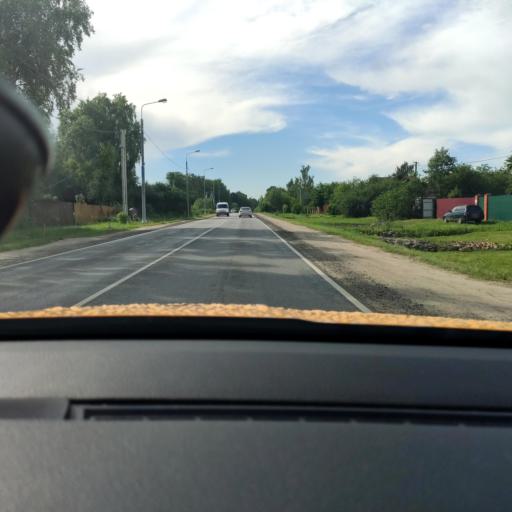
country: RU
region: Moskovskaya
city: Zhilevo
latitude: 54.9467
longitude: 38.0145
